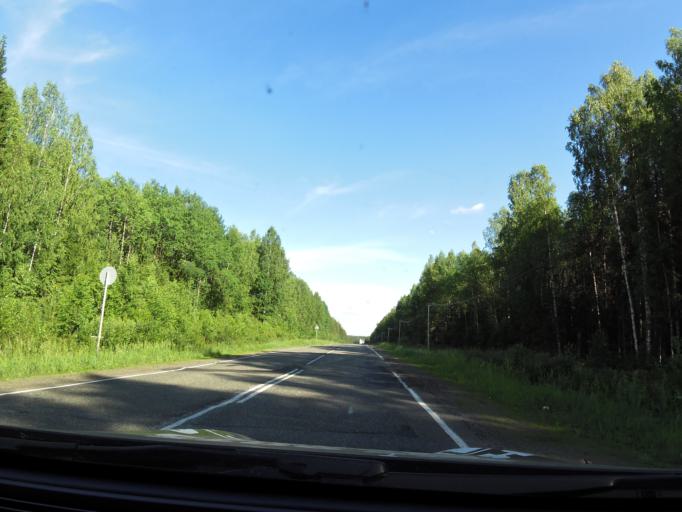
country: RU
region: Kirov
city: Dubrovka
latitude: 58.9117
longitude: 51.1708
